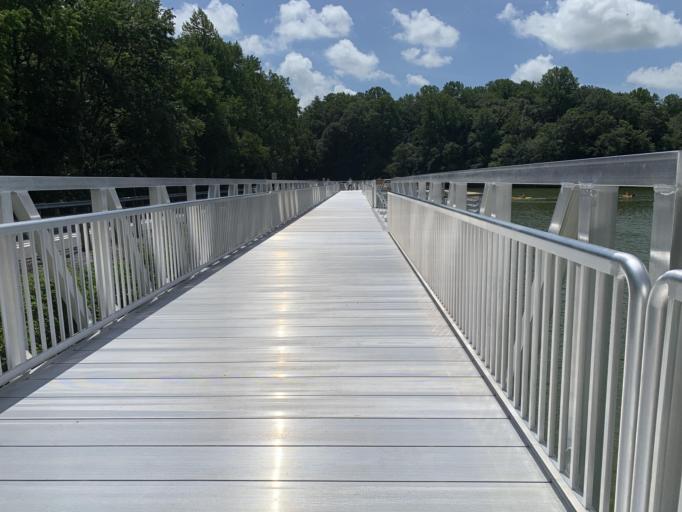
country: US
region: Delaware
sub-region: Kent County
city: Riverview
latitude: 38.9823
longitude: -75.5303
